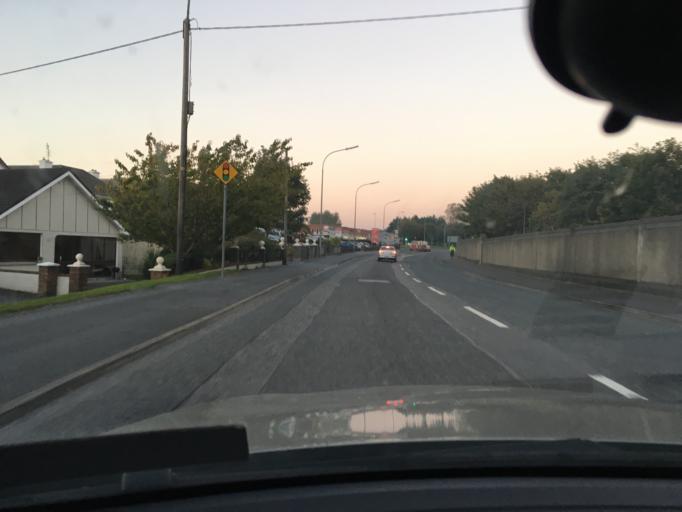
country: IE
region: Connaught
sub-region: County Galway
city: Gaillimh
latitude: 53.2845
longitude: -9.0349
